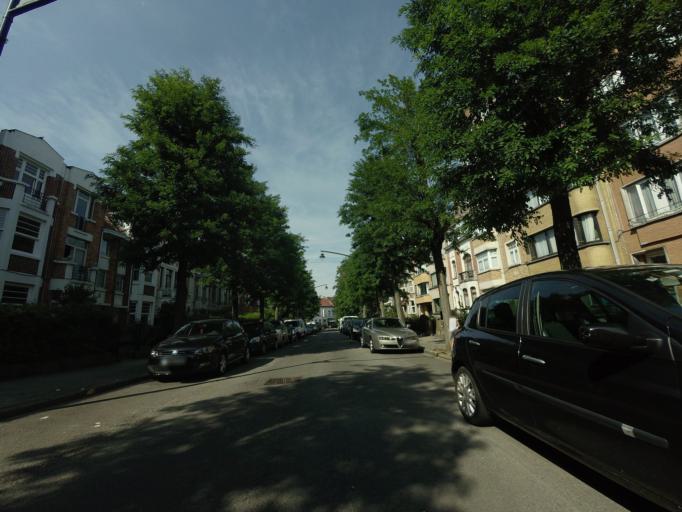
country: BE
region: Brussels Capital
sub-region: Bruxelles-Capitale
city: Brussels
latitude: 50.8767
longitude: 4.3452
